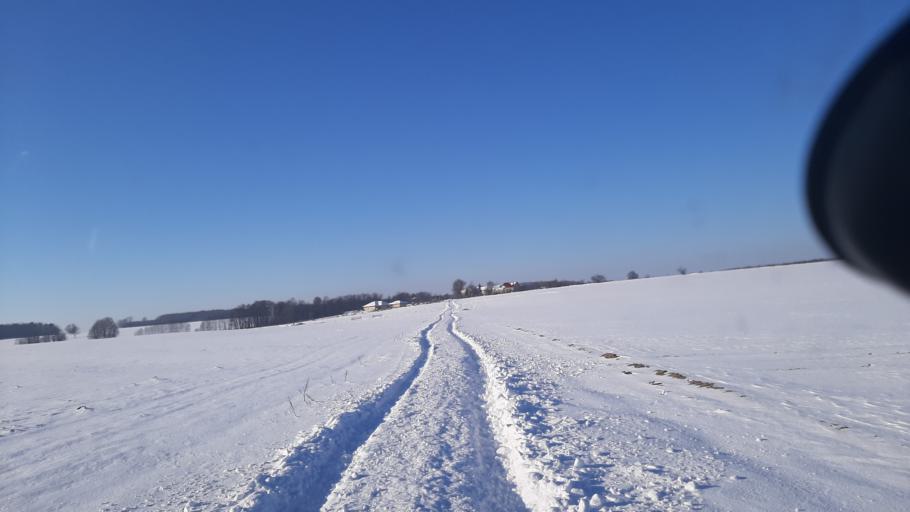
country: PL
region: Lublin Voivodeship
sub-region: Powiat lubelski
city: Jastkow
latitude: 51.3828
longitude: 22.4239
